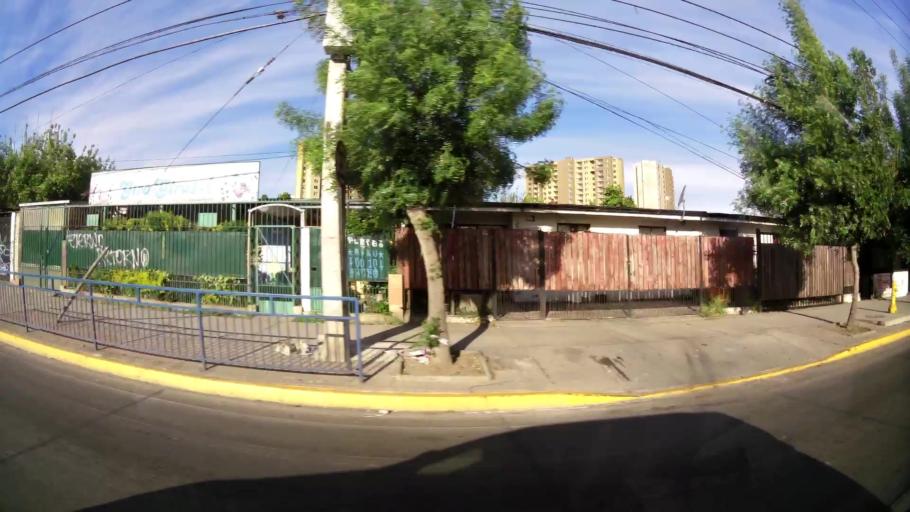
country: CL
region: Santiago Metropolitan
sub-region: Provincia de Santiago
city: Lo Prado
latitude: -33.4597
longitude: -70.7053
